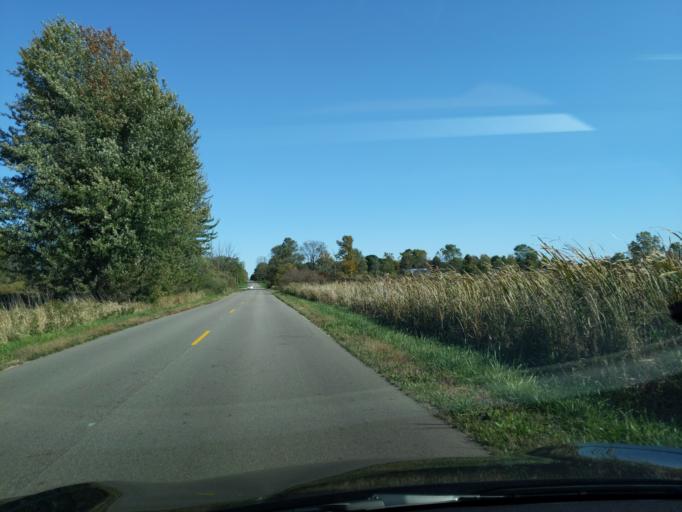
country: US
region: Michigan
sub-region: Eaton County
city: Potterville
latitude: 42.6401
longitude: -84.7616
